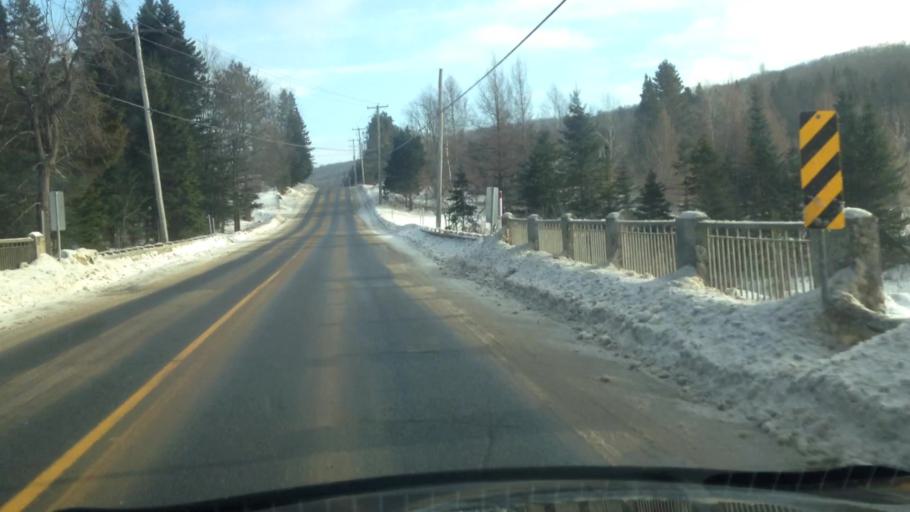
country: CA
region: Quebec
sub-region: Laurentides
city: Sainte-Agathe-des-Monts
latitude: 45.9254
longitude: -74.3958
